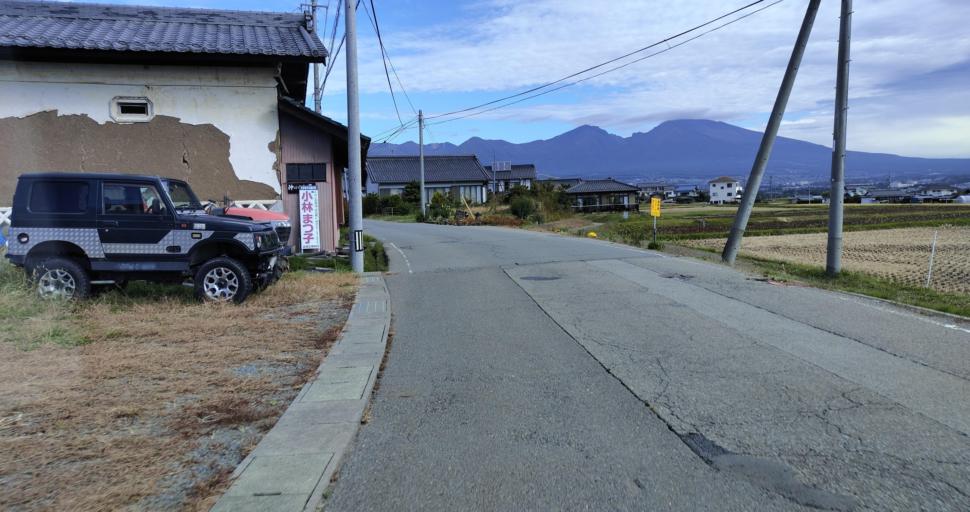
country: JP
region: Nagano
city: Komoro
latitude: 36.2716
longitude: 138.4060
